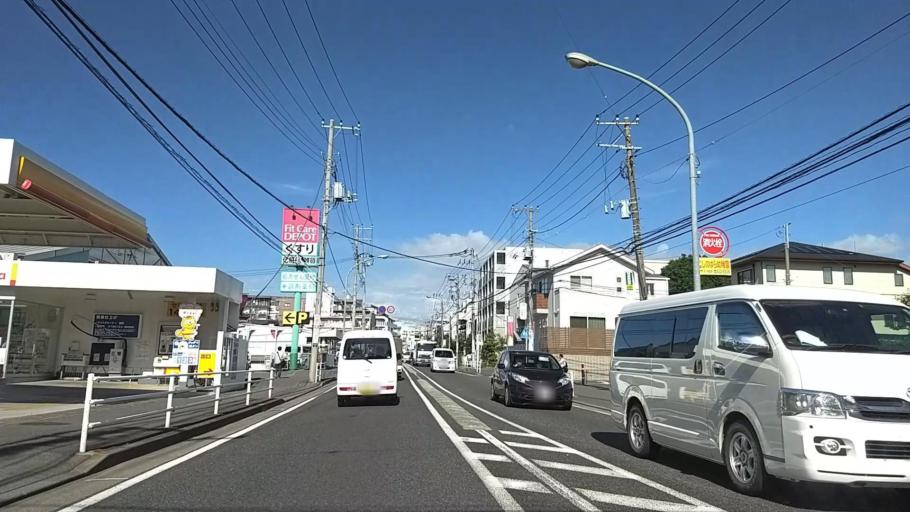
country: JP
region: Kanagawa
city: Yokohama
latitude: 35.4968
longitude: 139.6169
